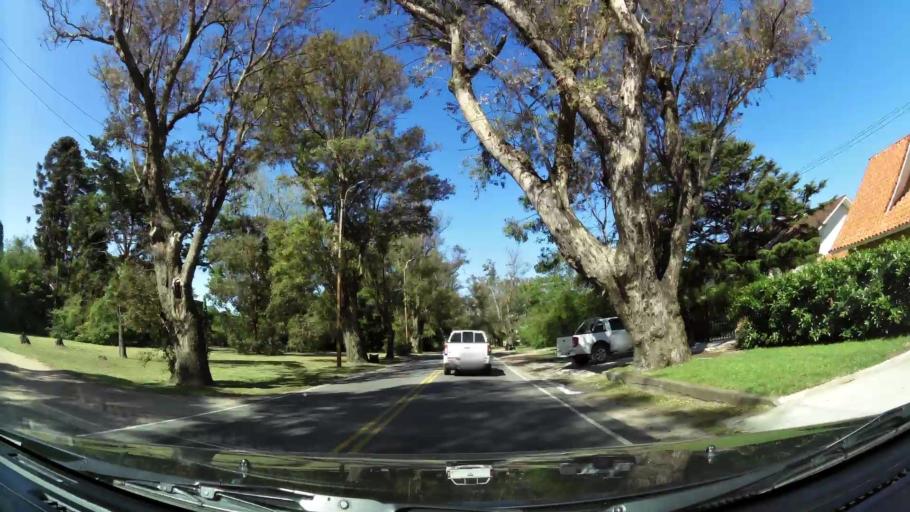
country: UY
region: Canelones
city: Barra de Carrasco
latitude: -34.8835
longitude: -56.0507
